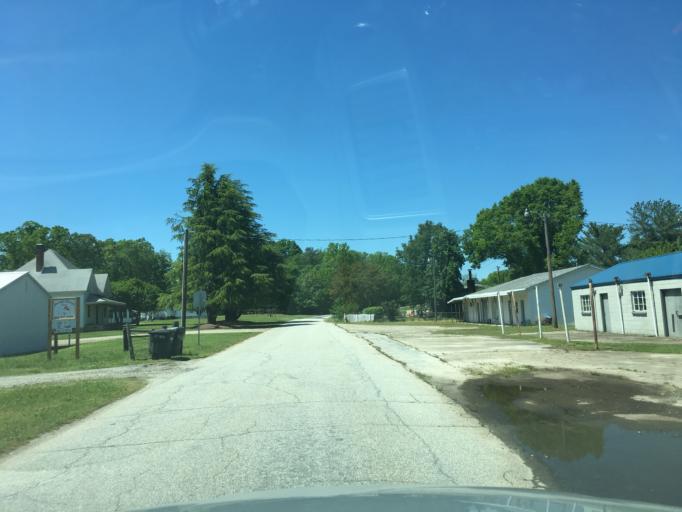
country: US
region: South Carolina
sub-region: Spartanburg County
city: Duncan
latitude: 34.8798
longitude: -82.1799
